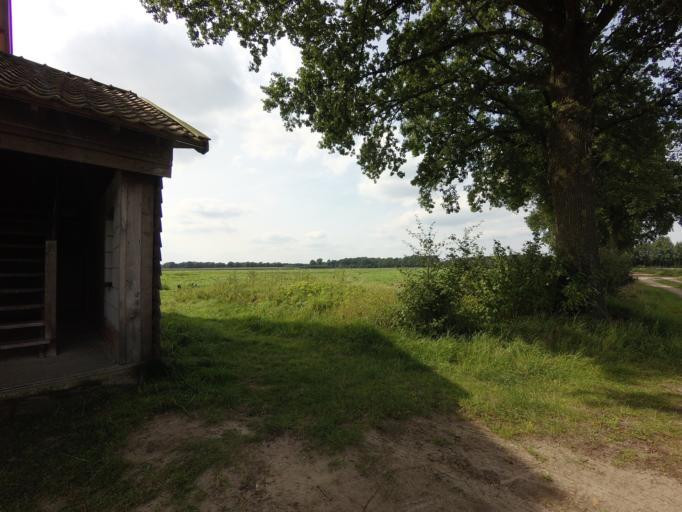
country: DE
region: Lower Saxony
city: Lage
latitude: 52.4274
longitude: 6.9499
